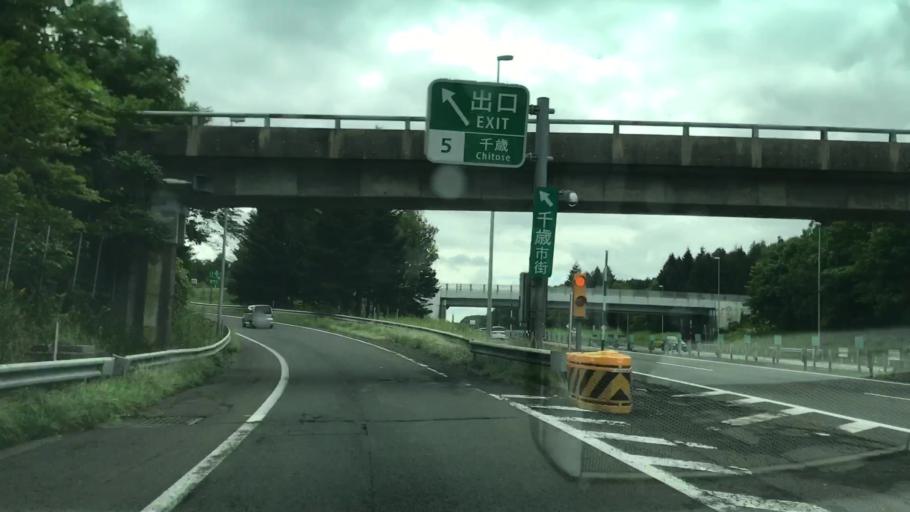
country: JP
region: Hokkaido
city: Chitose
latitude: 42.8130
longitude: 141.6206
